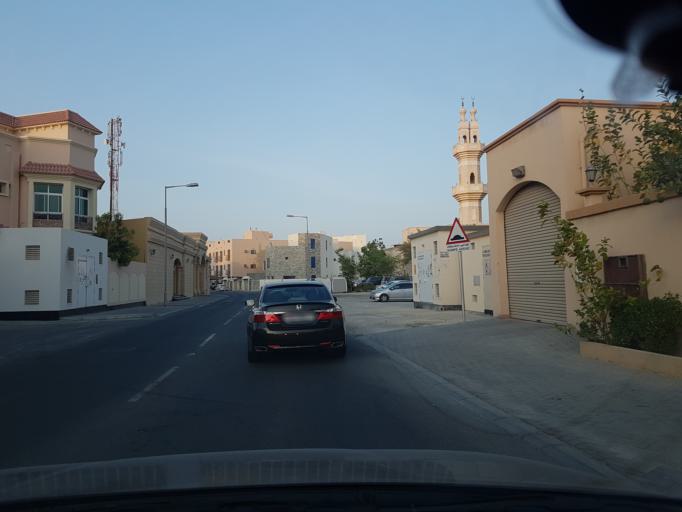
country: BH
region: Muharraq
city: Al Muharraq
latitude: 26.2763
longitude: 50.6092
